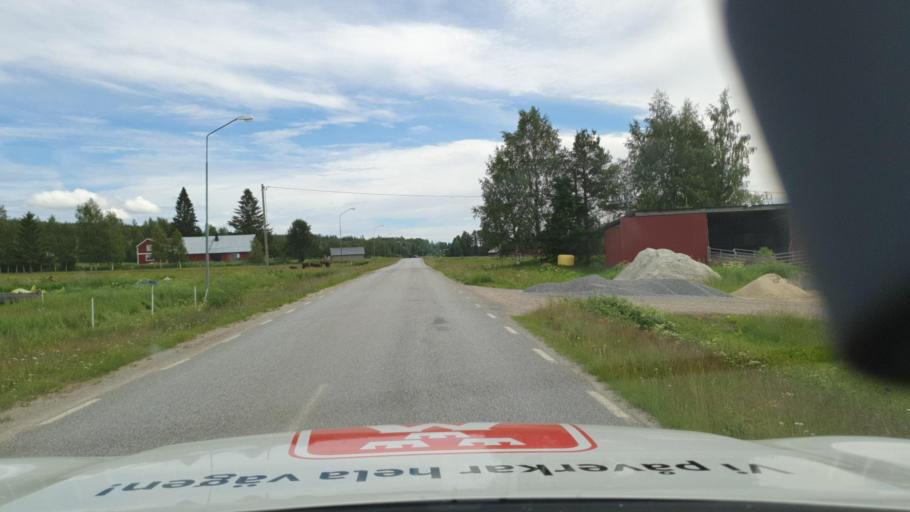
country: SE
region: Vaesterbotten
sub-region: Skelleftea Kommun
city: Burea
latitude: 64.5057
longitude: 21.0086
